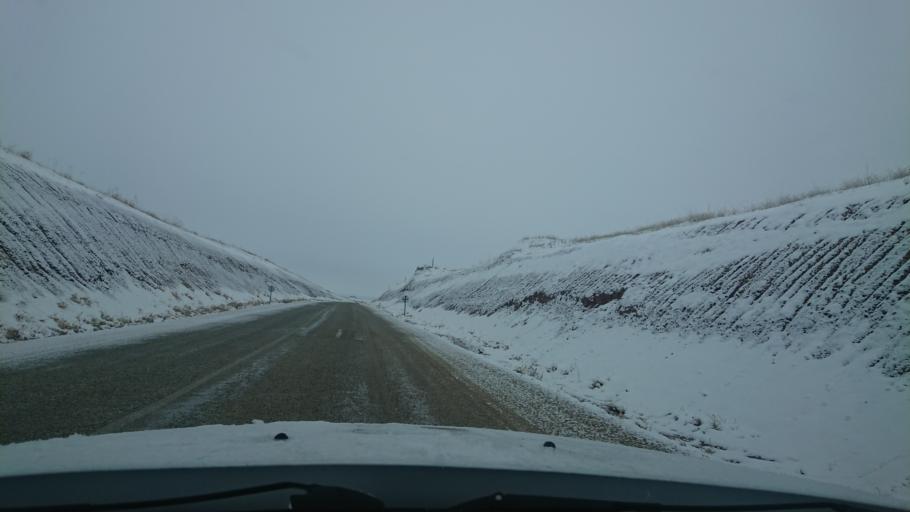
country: TR
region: Aksaray
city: Agacoren
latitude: 38.7729
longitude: 33.8693
